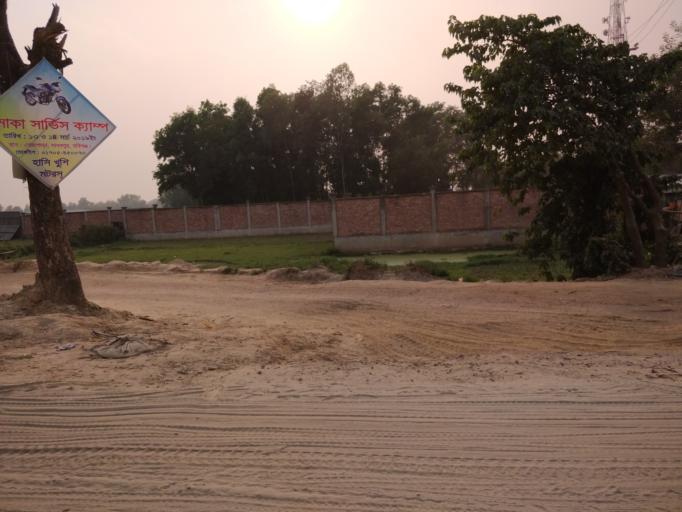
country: BD
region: Sylhet
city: Habiganj
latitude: 24.1484
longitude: 91.3514
